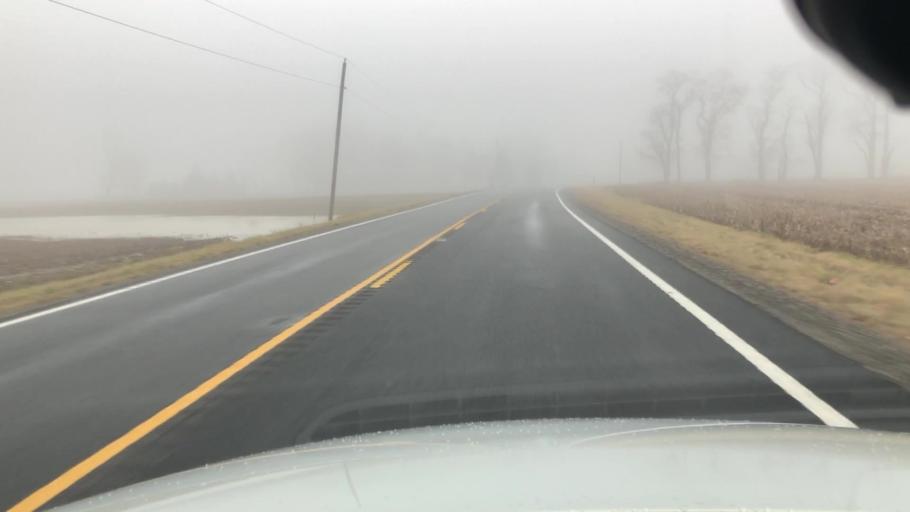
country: US
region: Ohio
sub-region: Logan County
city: Russells Point
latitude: 40.5711
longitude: -83.8469
